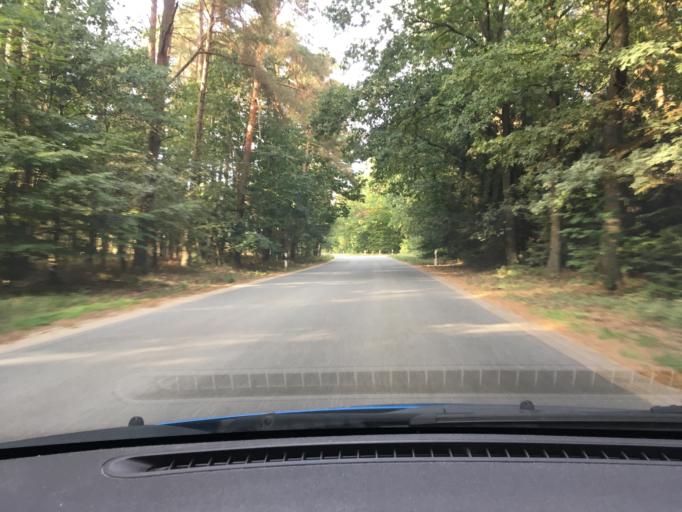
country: DE
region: Lower Saxony
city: Soltau
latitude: 52.9534
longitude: 9.9087
